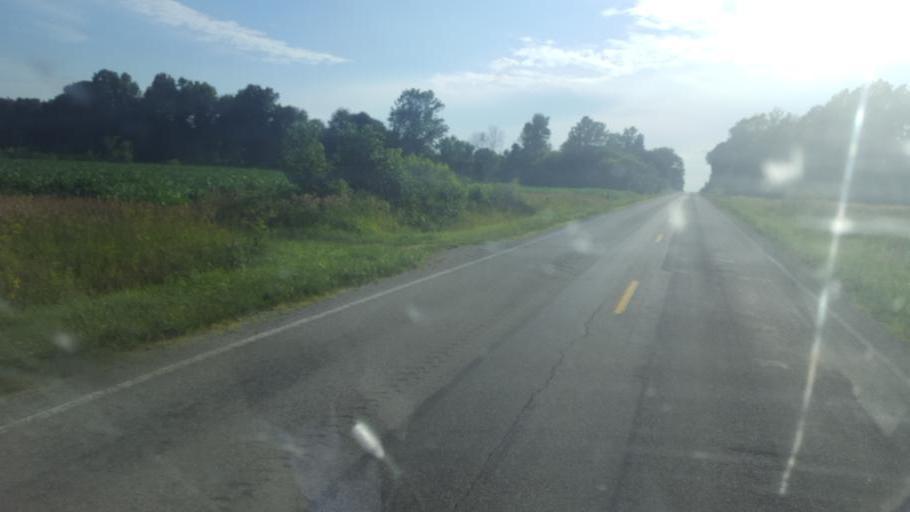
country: US
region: Ohio
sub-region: Ashland County
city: Ashland
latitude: 40.7726
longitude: -82.3112
